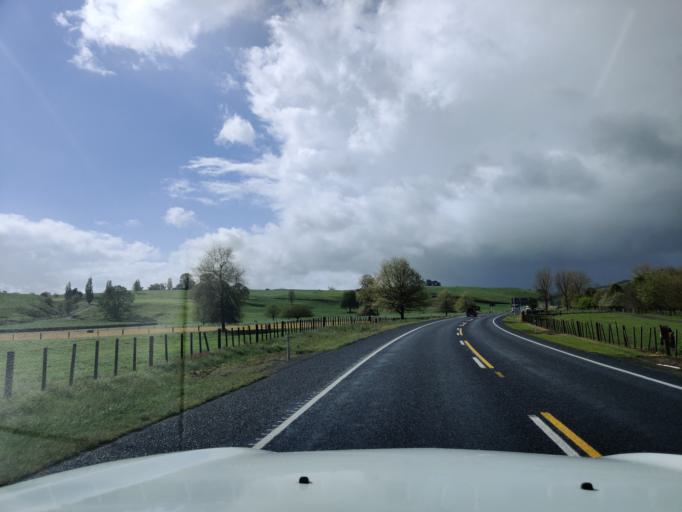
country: NZ
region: Waikato
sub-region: Matamata-Piako District
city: Matamata
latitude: -37.9443
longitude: 175.6705
